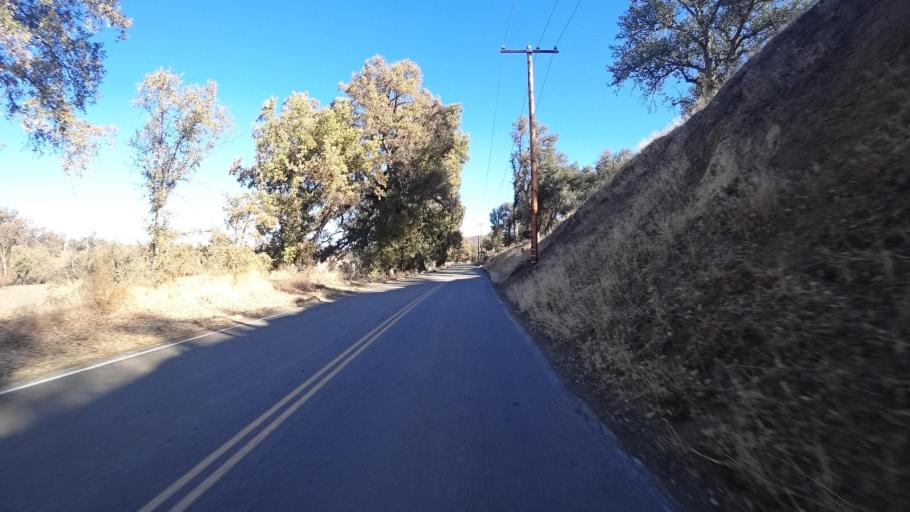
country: US
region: California
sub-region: Kern County
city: Alta Sierra
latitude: 35.7376
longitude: -118.7187
